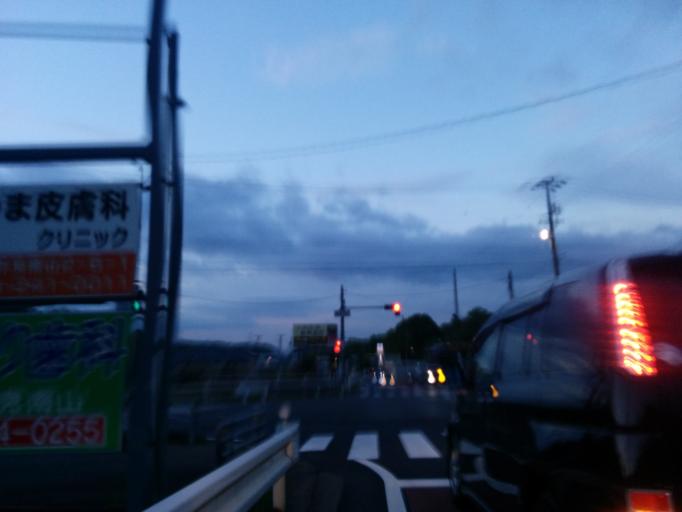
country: JP
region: Gifu
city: Kakamigahara
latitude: 35.4548
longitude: 136.8885
